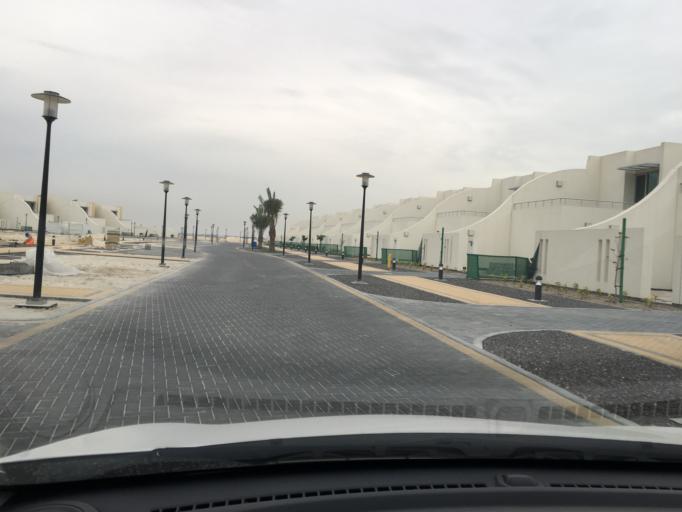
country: BH
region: Central Governorate
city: Dar Kulayb
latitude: 25.8296
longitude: 50.6049
